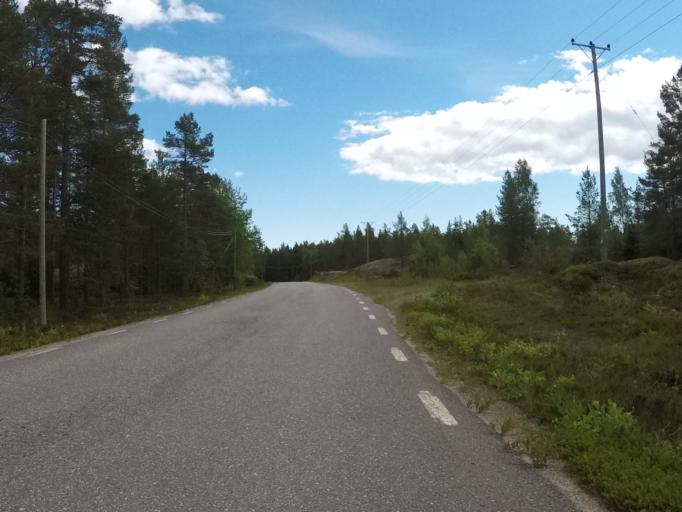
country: SE
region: Vaesterbotten
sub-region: Robertsfors Kommun
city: Robertsfors
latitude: 63.9905
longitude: 20.8242
